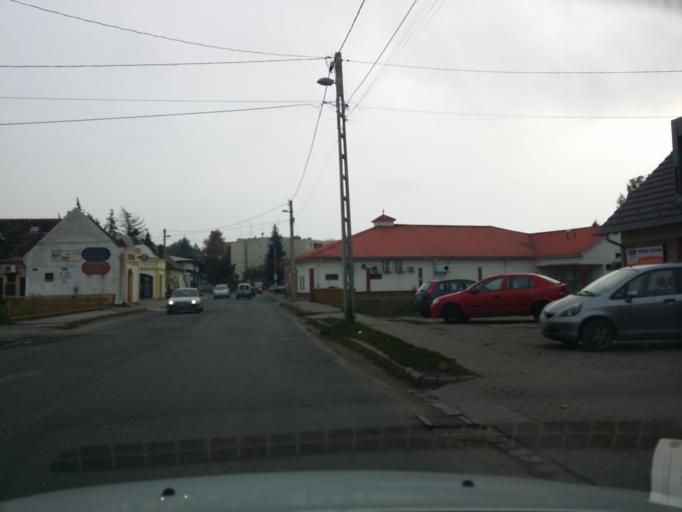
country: HU
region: Pest
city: Pecel
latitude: 47.4926
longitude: 19.3425
